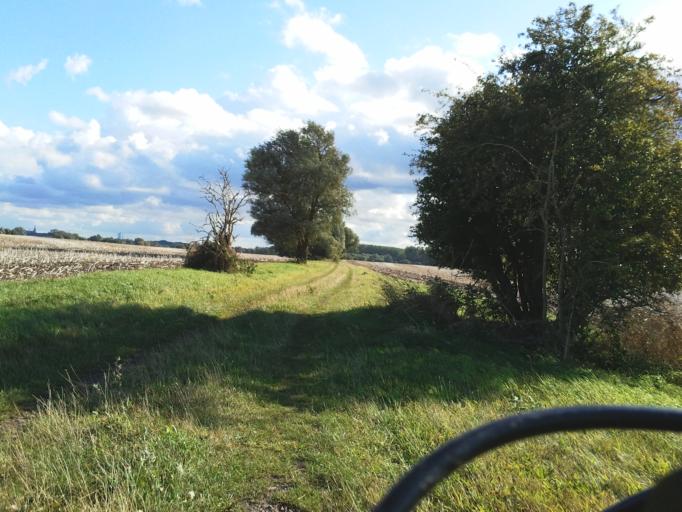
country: DE
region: Mecklenburg-Vorpommern
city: Dierkow-West
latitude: 54.1297
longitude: 12.1158
